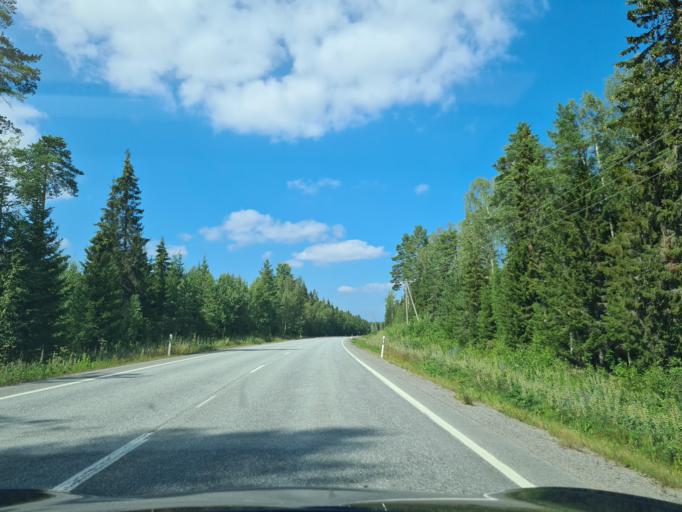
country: FI
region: Ostrobothnia
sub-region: Vaasa
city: Vaasa
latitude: 63.1731
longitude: 21.5799
